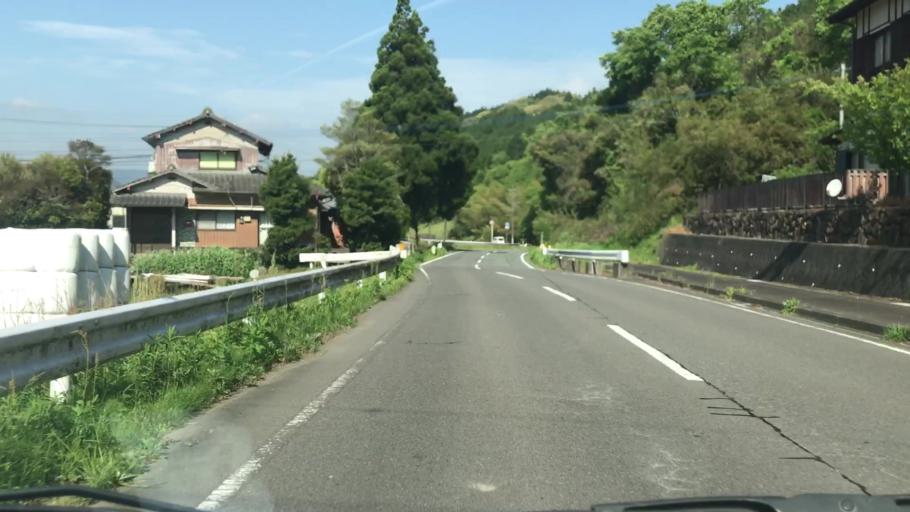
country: JP
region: Saga Prefecture
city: Takeocho-takeo
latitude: 33.2149
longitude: 129.9896
